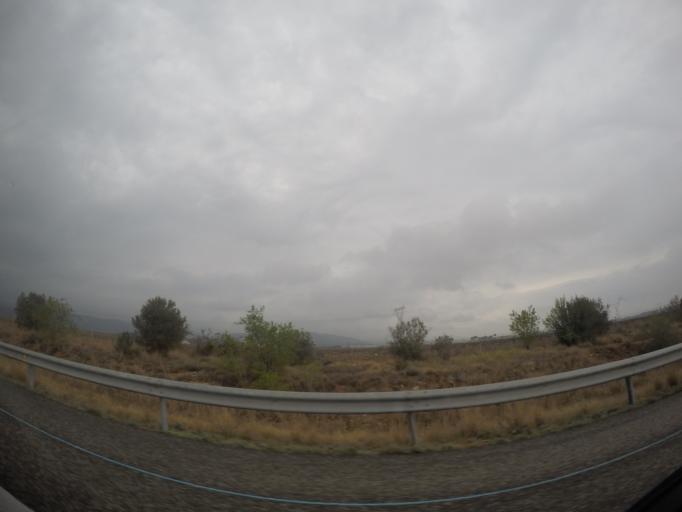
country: ES
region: Catalonia
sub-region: Provincia de Tarragona
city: Santa Oliva
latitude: 41.2729
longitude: 1.5257
